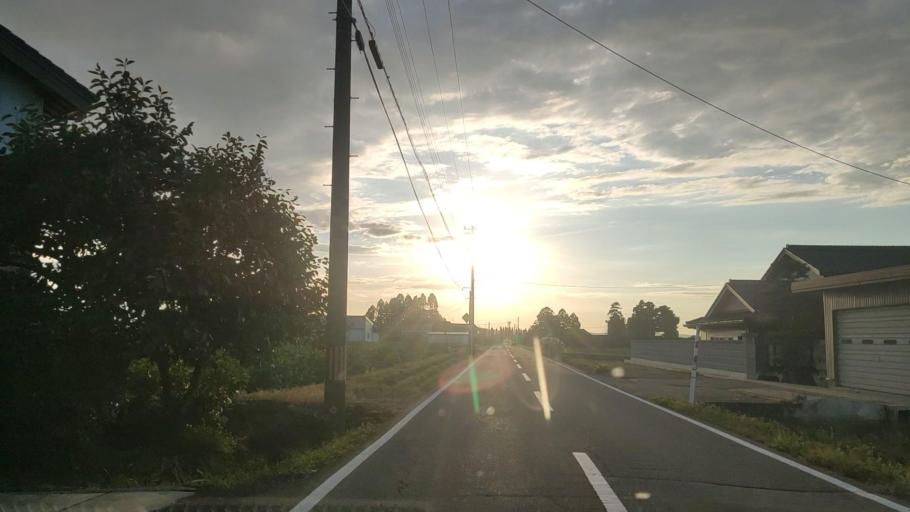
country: JP
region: Toyama
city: Nanto-shi
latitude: 36.5944
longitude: 136.9590
